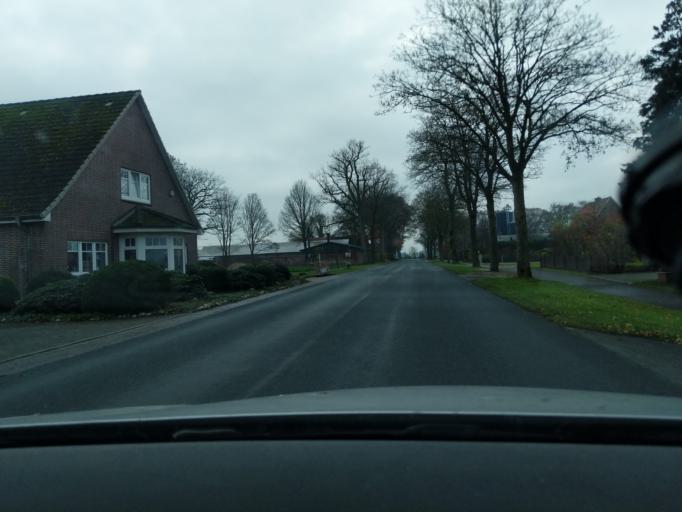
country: DE
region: Lower Saxony
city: Ahlerstedt
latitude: 53.3950
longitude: 9.4871
